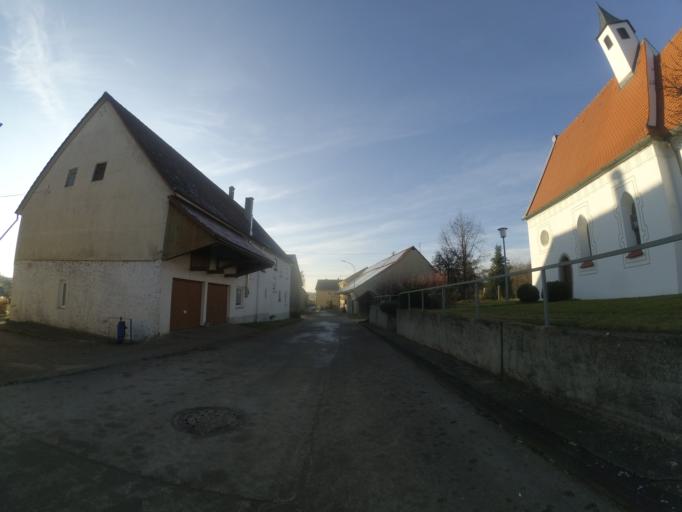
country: DE
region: Baden-Wuerttemberg
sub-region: Tuebingen Region
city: Dornstadt
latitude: 48.4628
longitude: 9.9091
